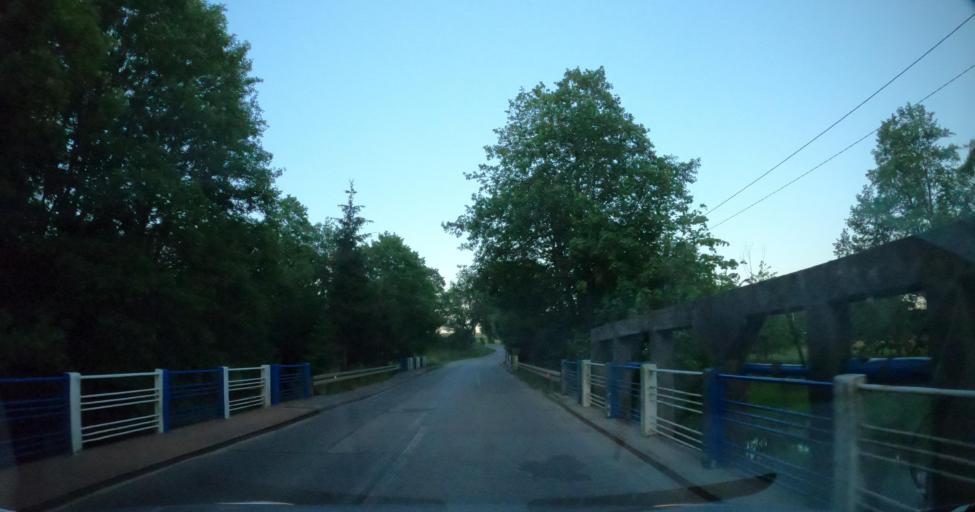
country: PL
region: Pomeranian Voivodeship
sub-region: Powiat wejherowski
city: Linia
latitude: 54.4629
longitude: 17.9763
